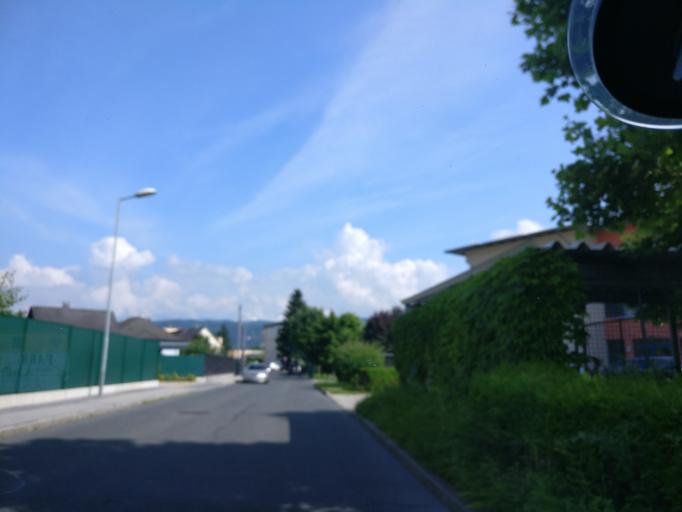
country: AT
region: Carinthia
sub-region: Klagenfurt am Woerthersee
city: Klagenfurt am Woerthersee
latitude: 46.6118
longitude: 14.2947
